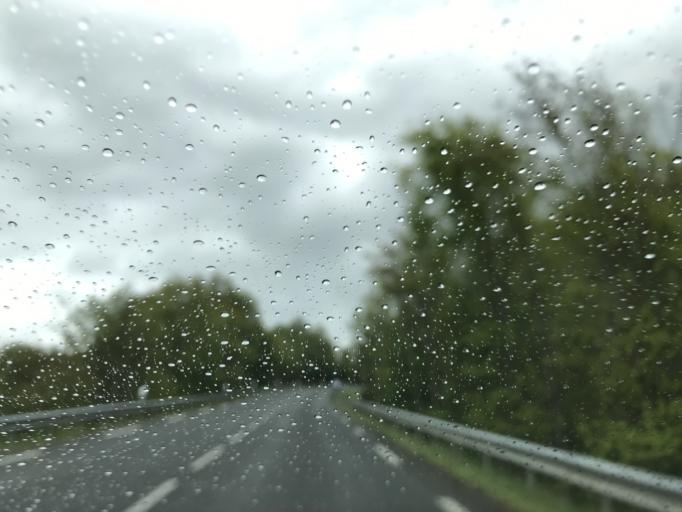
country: FR
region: Auvergne
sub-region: Departement du Puy-de-Dome
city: Billom
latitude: 45.6995
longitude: 3.4239
